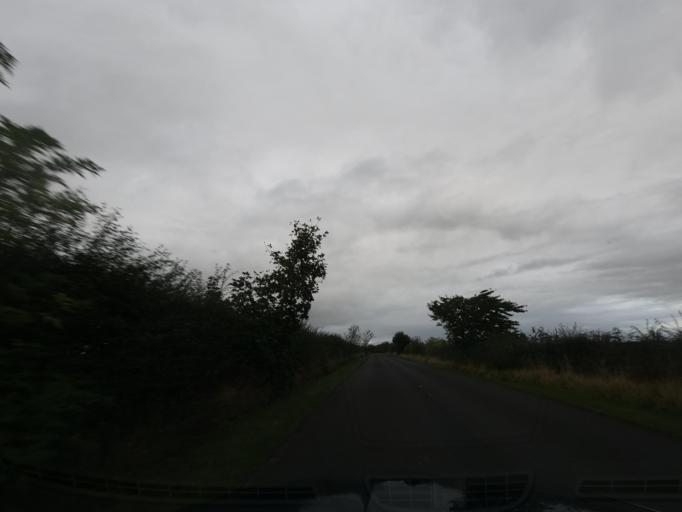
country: GB
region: England
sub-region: Northumberland
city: Ford
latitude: 55.6866
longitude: -2.0861
